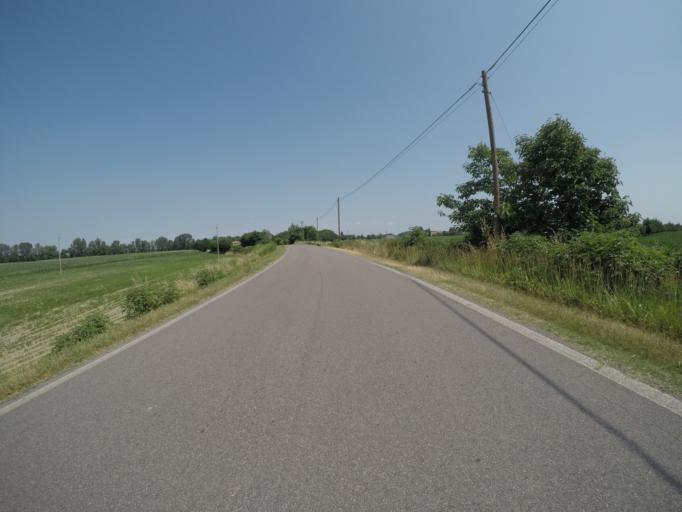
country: IT
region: Veneto
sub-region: Provincia di Rovigo
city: Fratta Polesine
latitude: 45.0031
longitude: 11.6544
